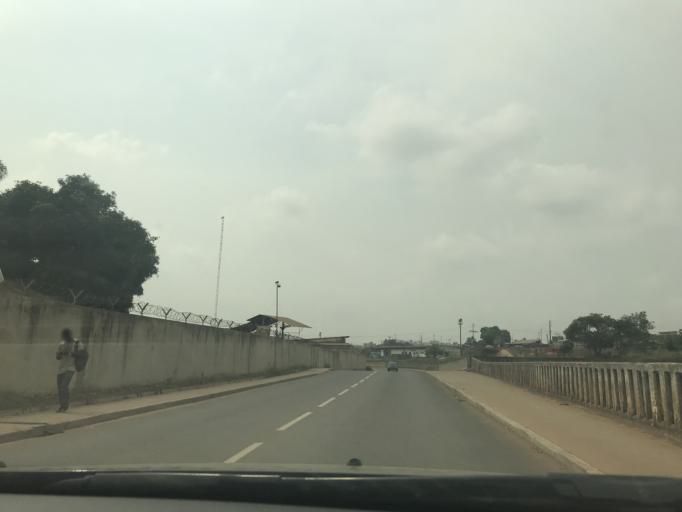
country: CM
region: Centre
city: Yaounde
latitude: 3.8400
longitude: 11.5131
